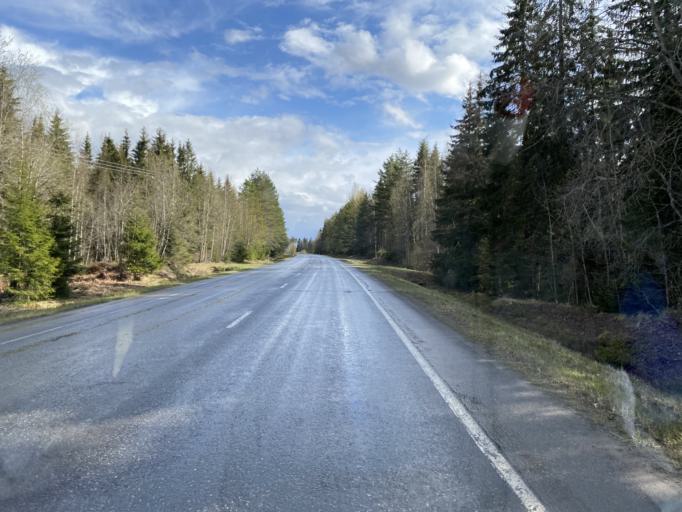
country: FI
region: Pirkanmaa
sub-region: Etelae-Pirkanmaa
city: Viiala
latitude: 61.2171
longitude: 23.7359
